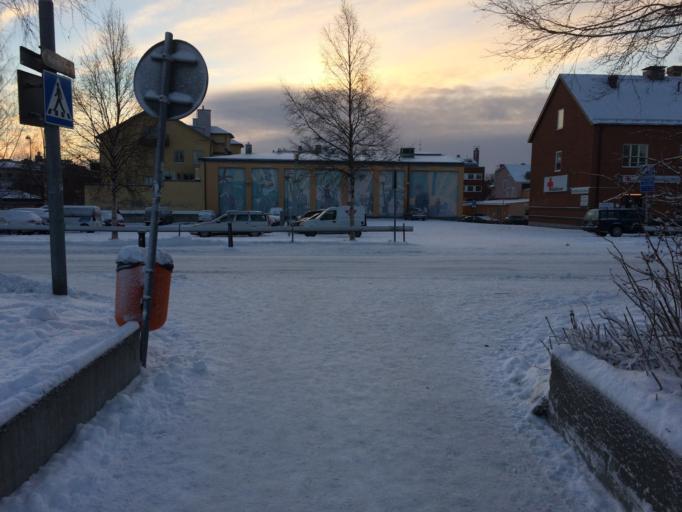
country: SE
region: Vaesterbotten
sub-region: Skelleftea Kommun
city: Skelleftea
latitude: 64.7533
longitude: 20.9532
